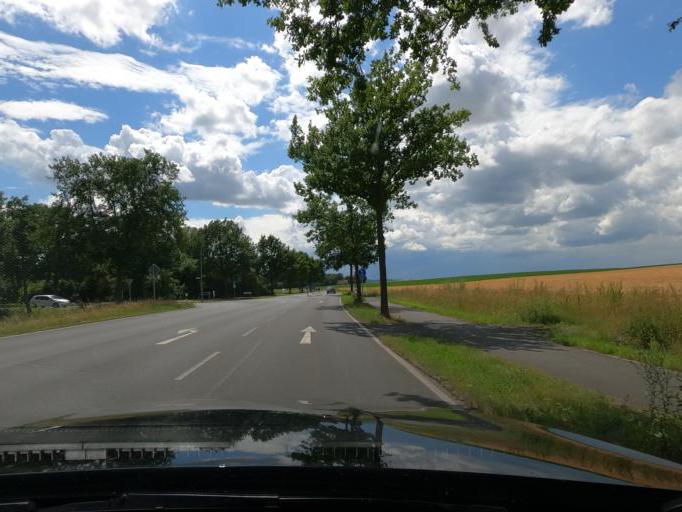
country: DE
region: Lower Saxony
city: Lengede
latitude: 52.1673
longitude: 10.3048
